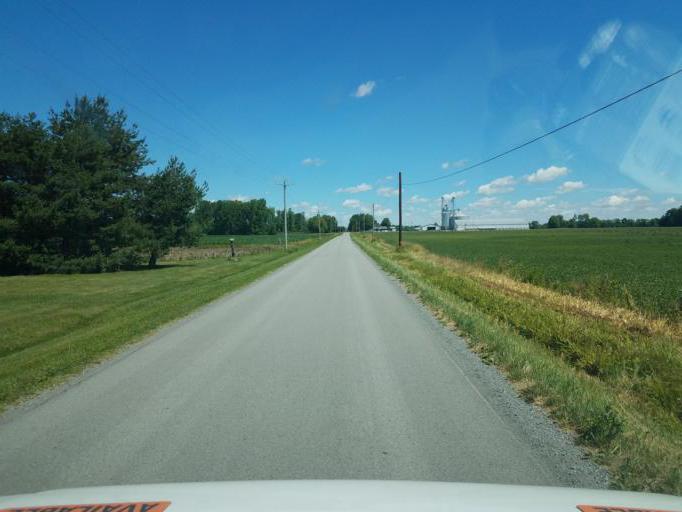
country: US
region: Ohio
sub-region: Morrow County
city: Cardington
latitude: 40.6027
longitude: -82.9379
